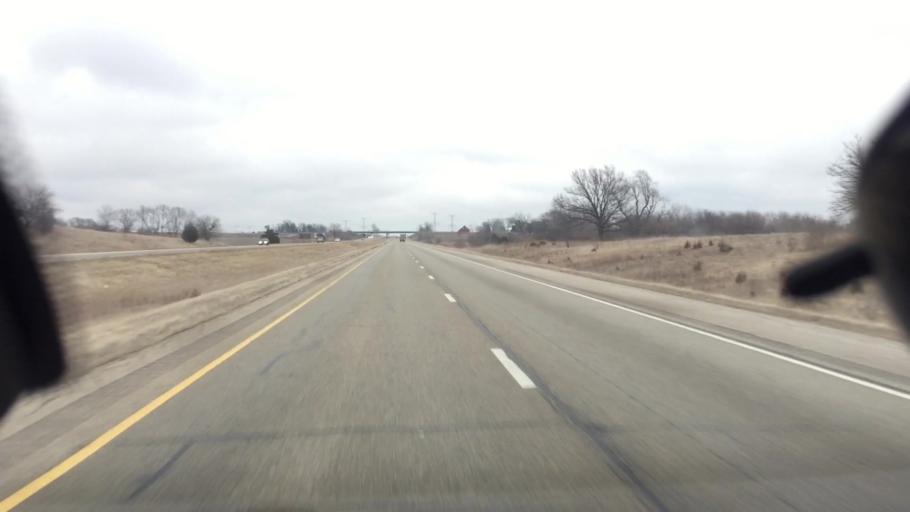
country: US
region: Illinois
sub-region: Tazewell County
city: Morton
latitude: 40.6215
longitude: -89.4152
